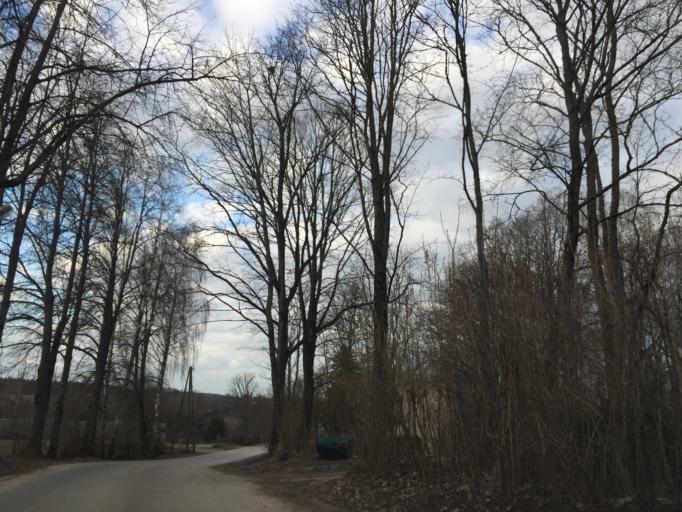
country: LV
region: Jaunjelgava
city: Jaunjelgava
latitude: 56.6118
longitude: 25.0715
